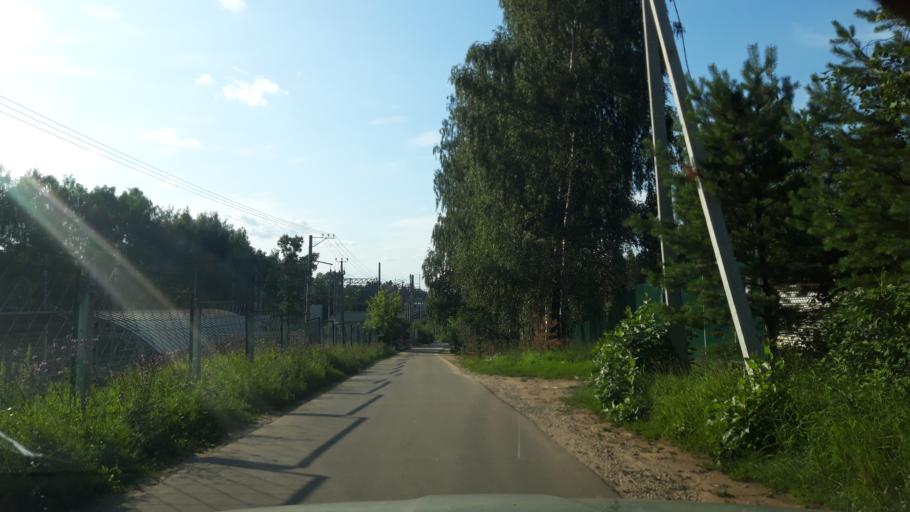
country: RU
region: Moskovskaya
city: Povarovo
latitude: 56.0640
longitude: 37.0771
